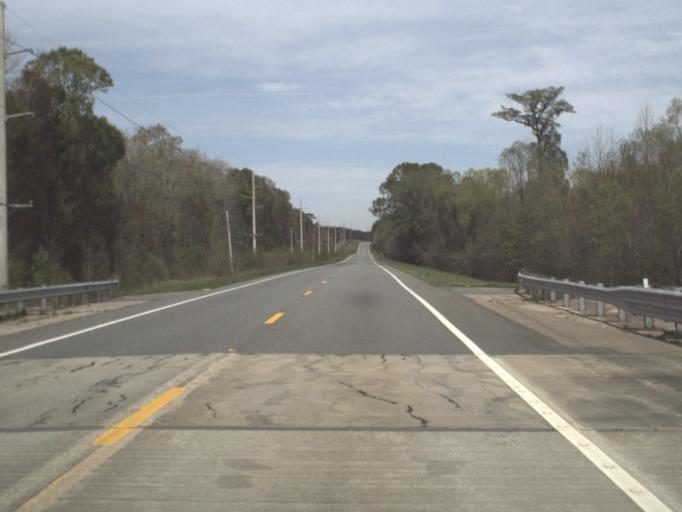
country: US
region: Alabama
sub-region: Houston County
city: Cottonwood
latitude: 30.9379
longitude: -85.2947
